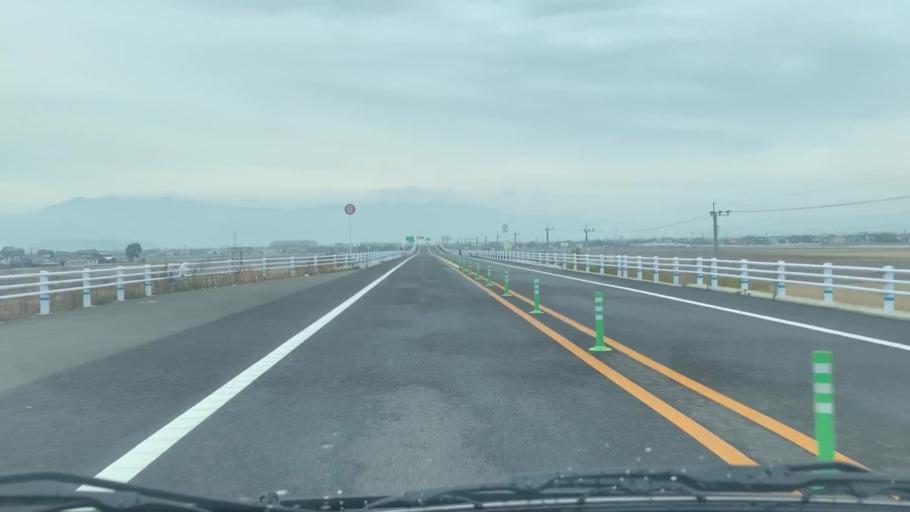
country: JP
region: Saga Prefecture
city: Saga-shi
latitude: 33.2108
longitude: 130.2148
